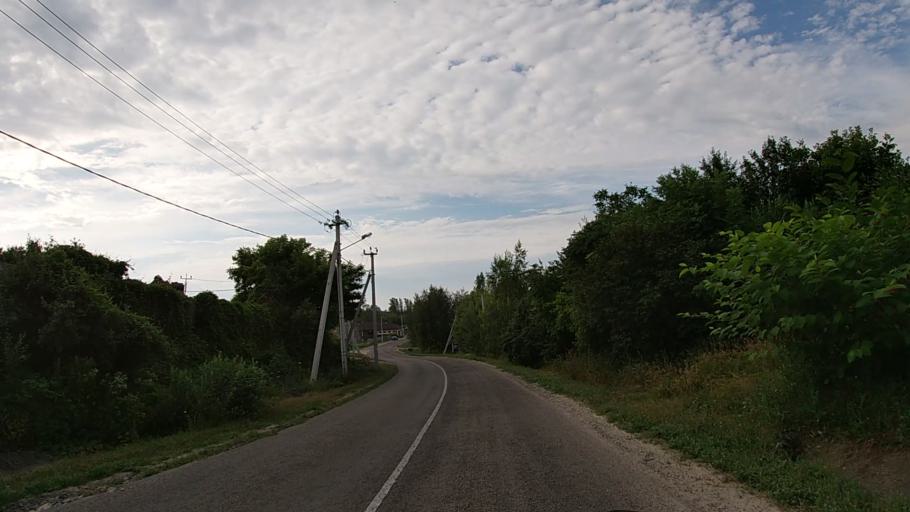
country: RU
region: Belgorod
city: Severnyy
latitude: 50.7127
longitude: 36.5960
